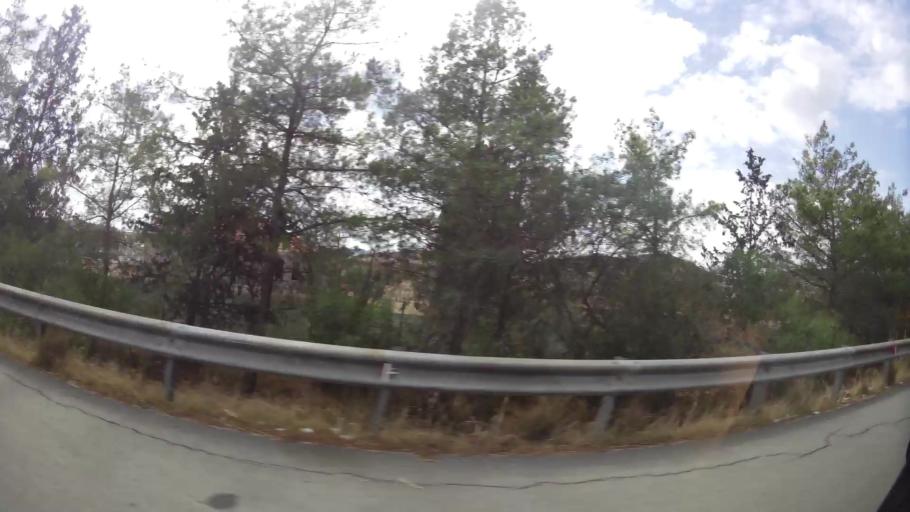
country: CY
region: Lefkosia
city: Lympia
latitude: 34.9971
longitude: 33.4359
